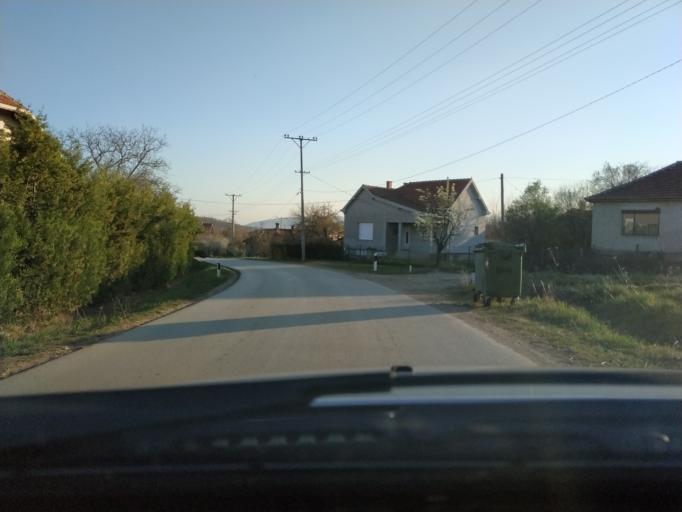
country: RS
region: Central Serbia
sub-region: Nisavski Okrug
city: Aleksinac
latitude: 43.4967
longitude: 21.7859
